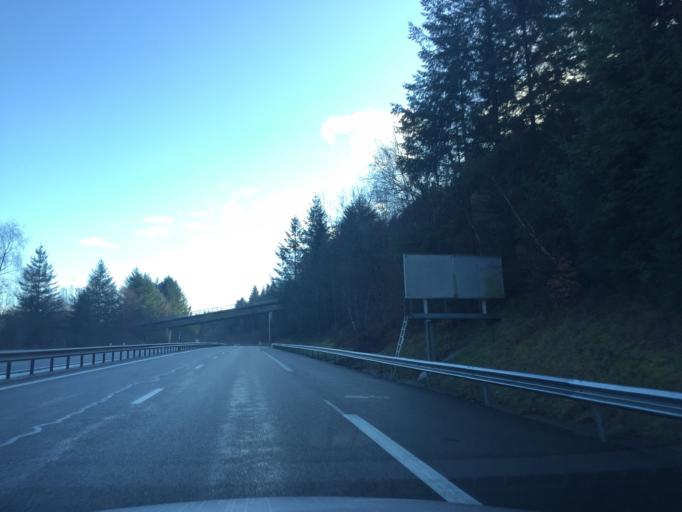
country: FR
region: Auvergne
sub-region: Departement du Puy-de-Dome
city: Chabreloche
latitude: 45.8532
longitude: 3.7267
